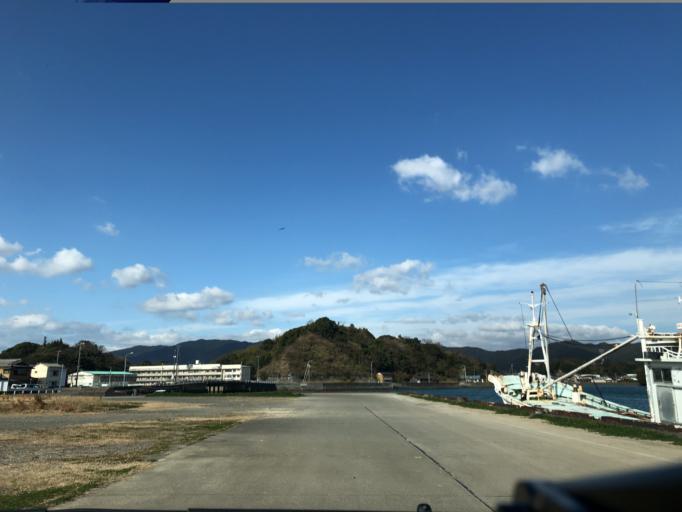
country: JP
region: Kochi
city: Sukumo
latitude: 32.9173
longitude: 132.7044
